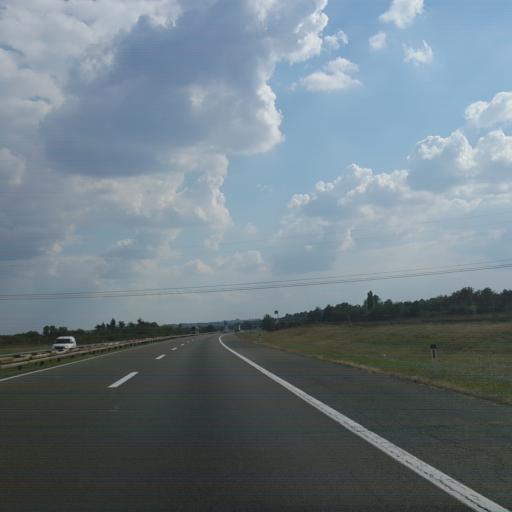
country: RS
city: Lugavcina
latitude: 44.5590
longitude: 20.9832
